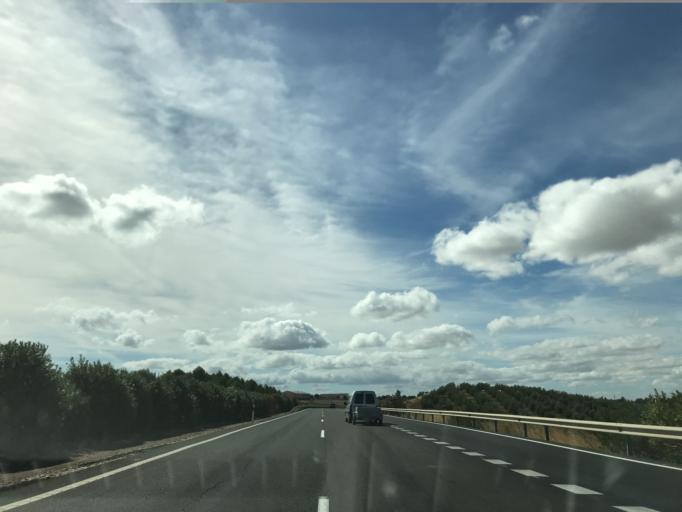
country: ES
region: Andalusia
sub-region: Province of Cordoba
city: La Victoria
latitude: 37.7208
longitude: -4.8615
